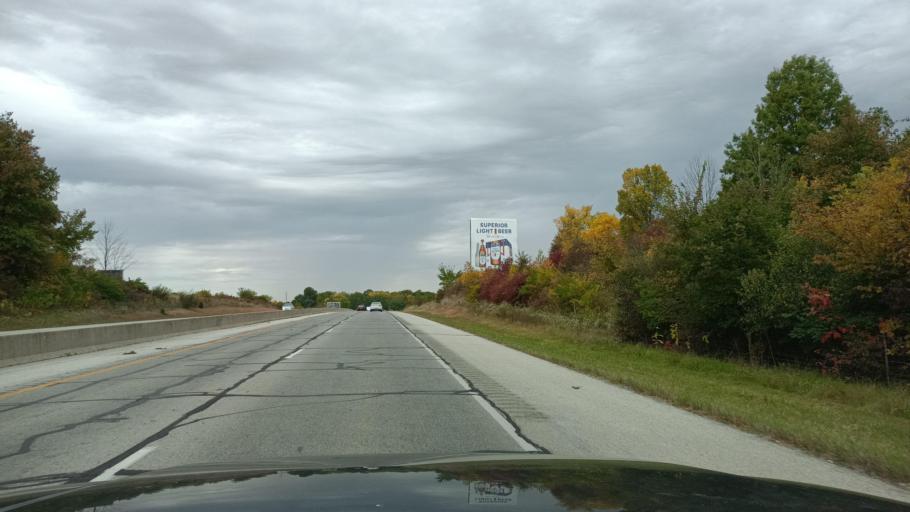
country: US
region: Indiana
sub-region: Delaware County
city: Yorktown
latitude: 40.2192
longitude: -85.5106
